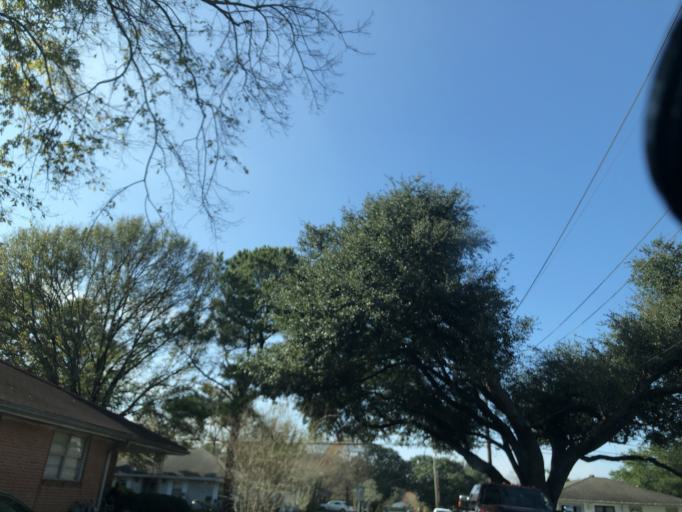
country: US
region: Louisiana
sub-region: Jefferson Parish
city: Metairie
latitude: 29.9911
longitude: -90.1503
